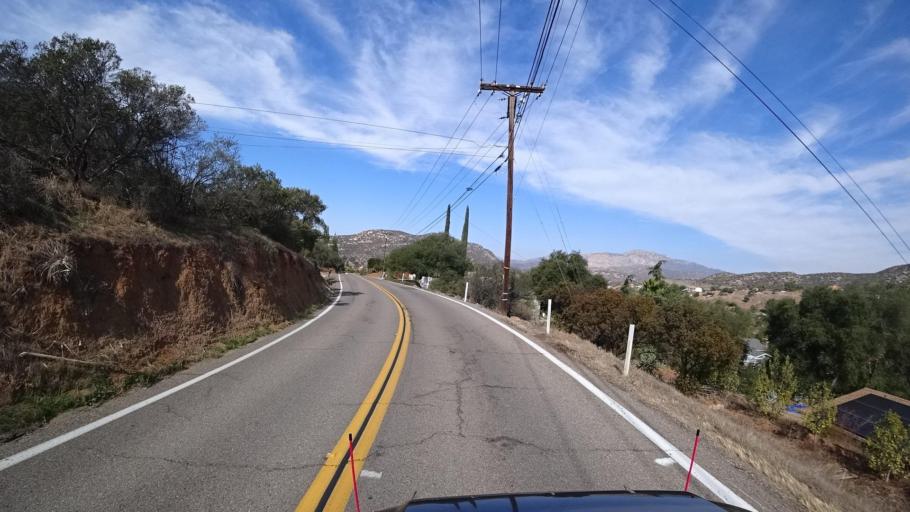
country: US
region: California
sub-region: San Diego County
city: Alpine
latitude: 32.8351
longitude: -116.7998
